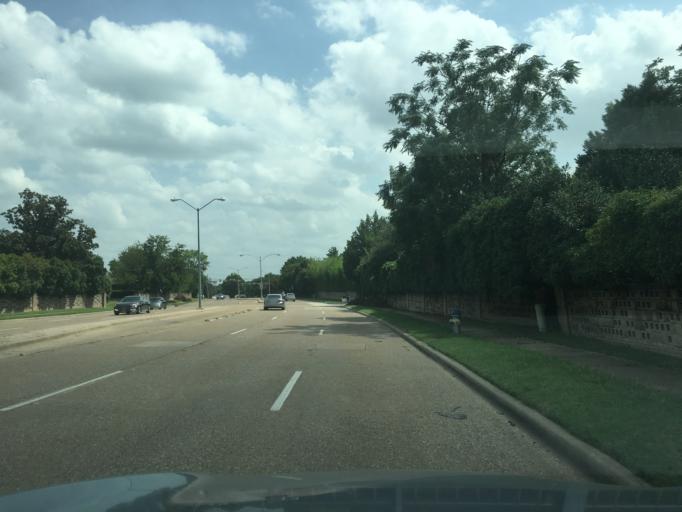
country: US
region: Texas
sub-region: Dallas County
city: University Park
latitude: 32.8971
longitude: -96.8196
